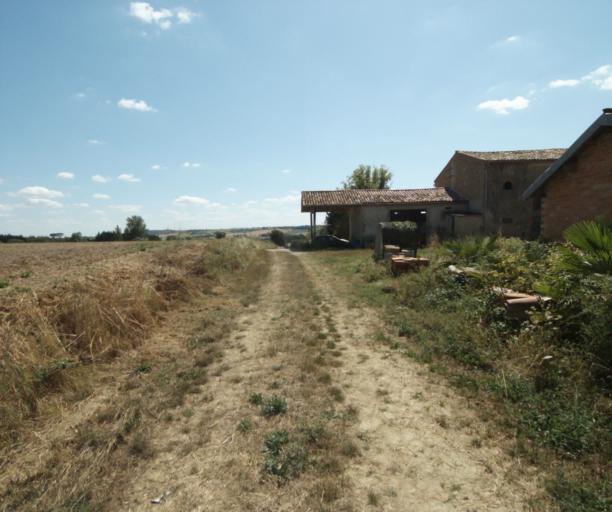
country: FR
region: Midi-Pyrenees
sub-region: Departement de la Haute-Garonne
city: Saint-Felix-Lauragais
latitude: 43.4953
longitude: 1.8833
